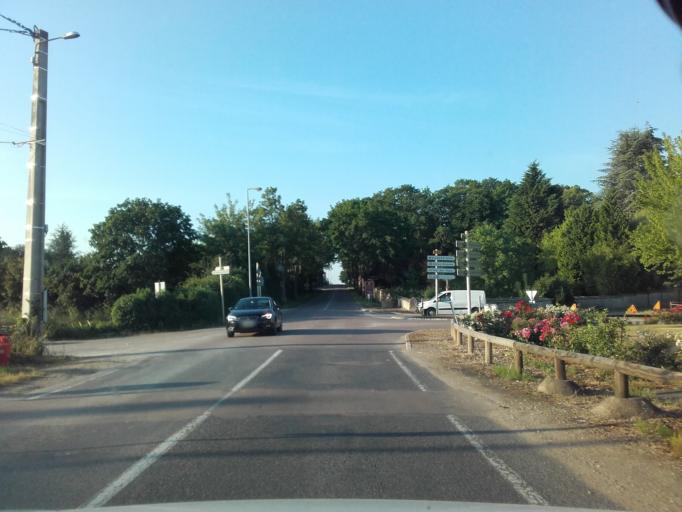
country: FR
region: Bourgogne
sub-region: Departement de Saone-et-Loire
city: Dracy-le-Fort
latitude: 46.8151
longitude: 4.7521
